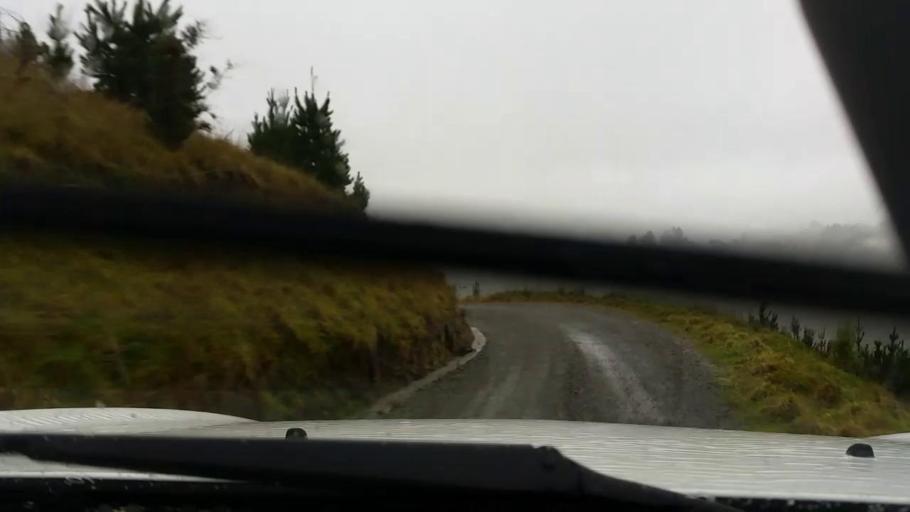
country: NZ
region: Wellington
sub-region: Masterton District
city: Masterton
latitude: -41.1975
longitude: 175.8113
